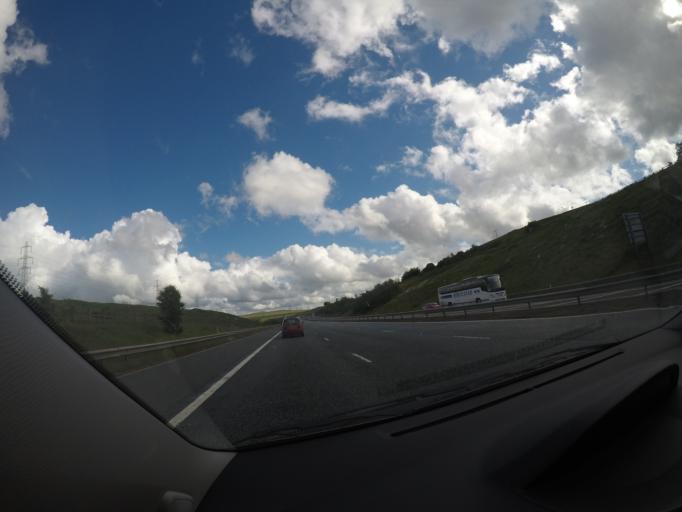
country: GB
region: Scotland
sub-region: South Lanarkshire
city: Douglas
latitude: 55.5554
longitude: -3.8015
